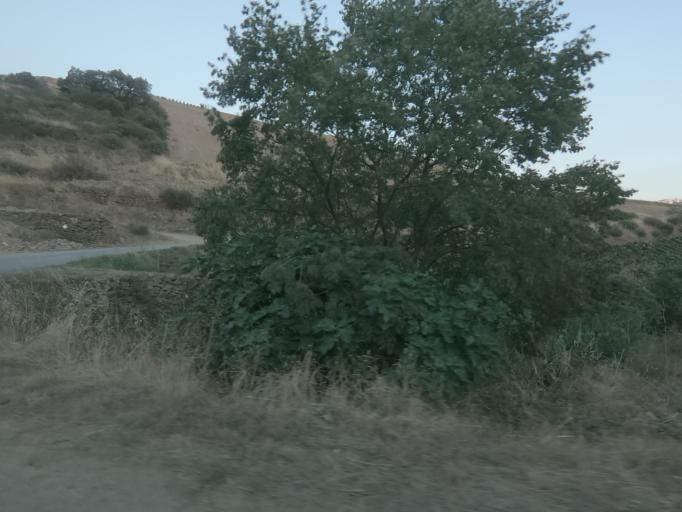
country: PT
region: Viseu
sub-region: Armamar
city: Armamar
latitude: 41.1469
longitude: -7.7018
